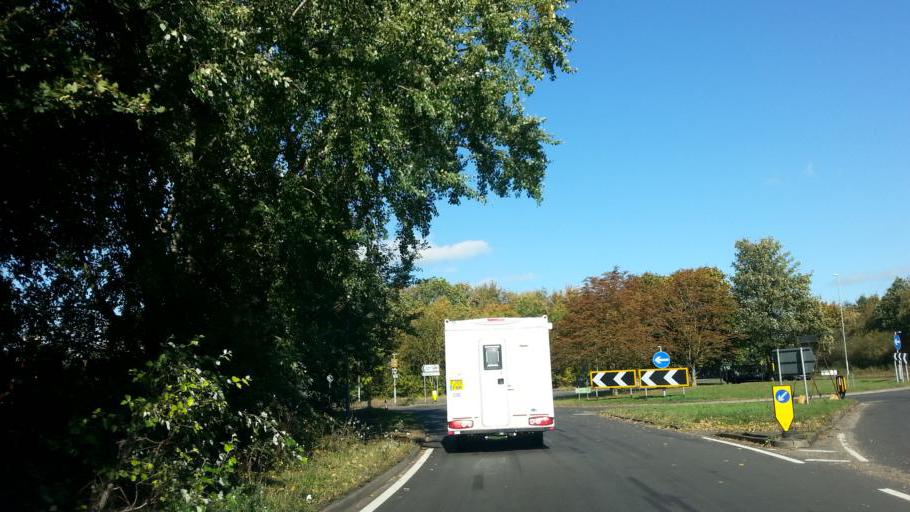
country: GB
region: England
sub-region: Northamptonshire
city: Oundle
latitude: 52.4879
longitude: -0.4596
